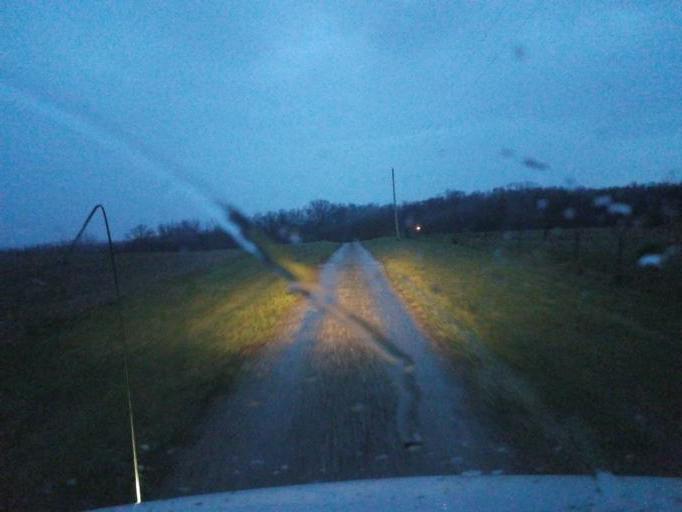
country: US
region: Ohio
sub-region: Knox County
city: Gambier
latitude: 40.3200
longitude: -82.4488
